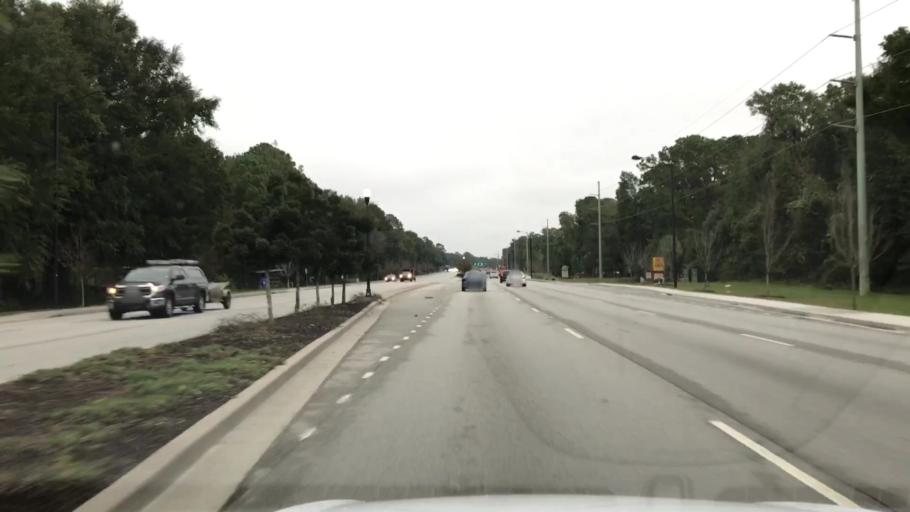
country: US
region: South Carolina
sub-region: Charleston County
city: Isle of Palms
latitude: 32.8677
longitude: -79.7824
